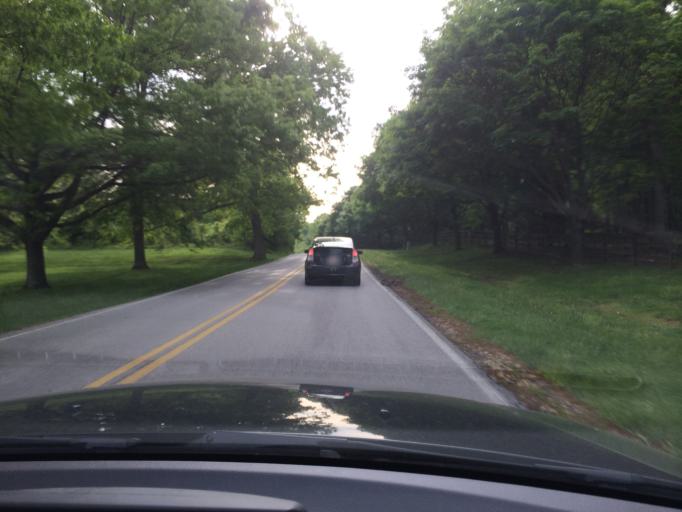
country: US
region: Maryland
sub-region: Howard County
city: Highland
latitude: 39.2030
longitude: -76.9649
